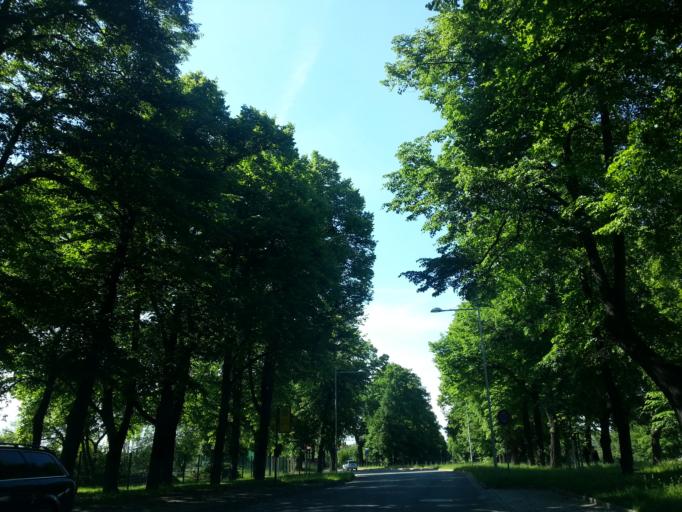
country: DE
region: Saxony
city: Dresden
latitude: 51.0658
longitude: 13.7252
